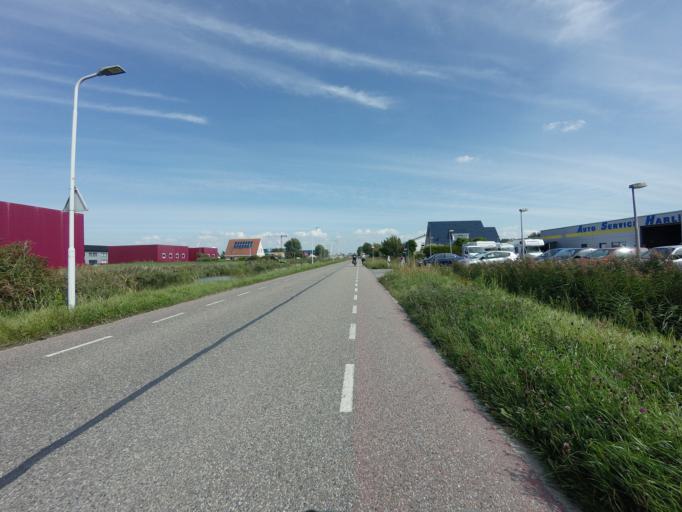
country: NL
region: Friesland
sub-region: Gemeente Harlingen
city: Harlingen
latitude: 53.1743
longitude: 5.4411
